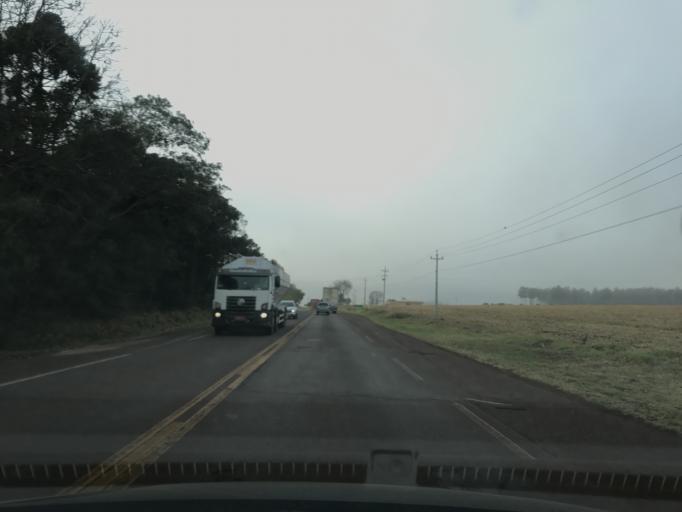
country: BR
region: Parana
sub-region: Toledo
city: Toledo
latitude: -24.6651
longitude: -53.6995
